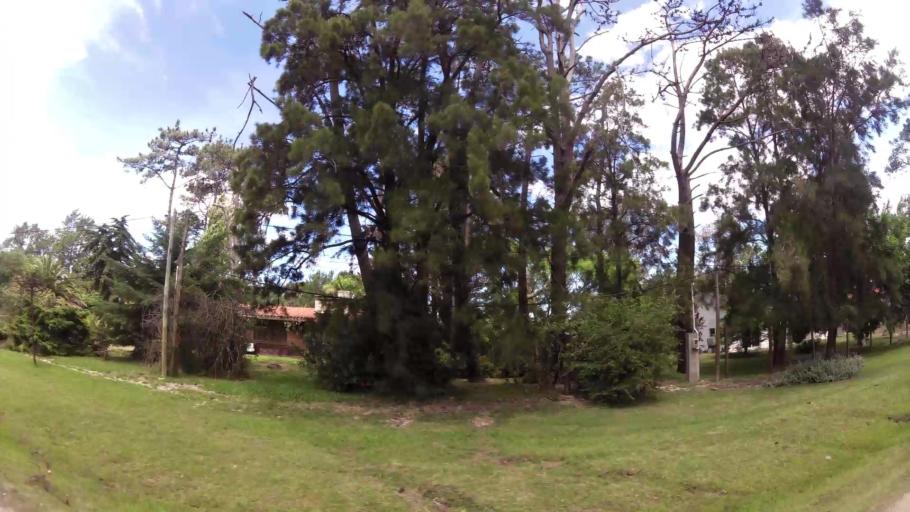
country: UY
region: Canelones
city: Empalme Olmos
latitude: -34.7966
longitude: -55.8871
